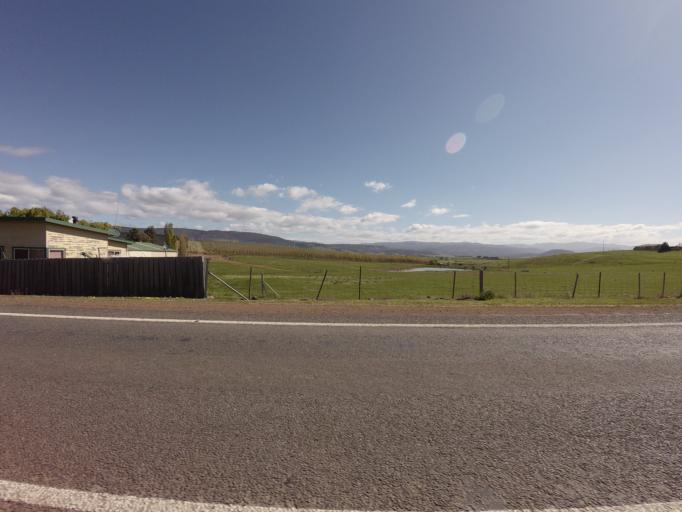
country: AU
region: Tasmania
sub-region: Derwent Valley
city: New Norfolk
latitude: -42.7073
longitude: 146.9448
